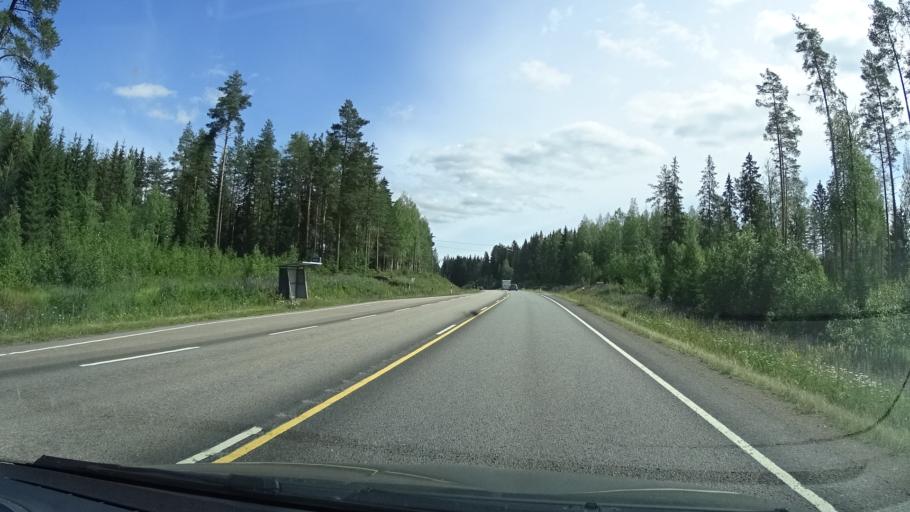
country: FI
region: Central Finland
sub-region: Jyvaeskylae
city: Muurame
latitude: 62.2668
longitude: 25.4980
